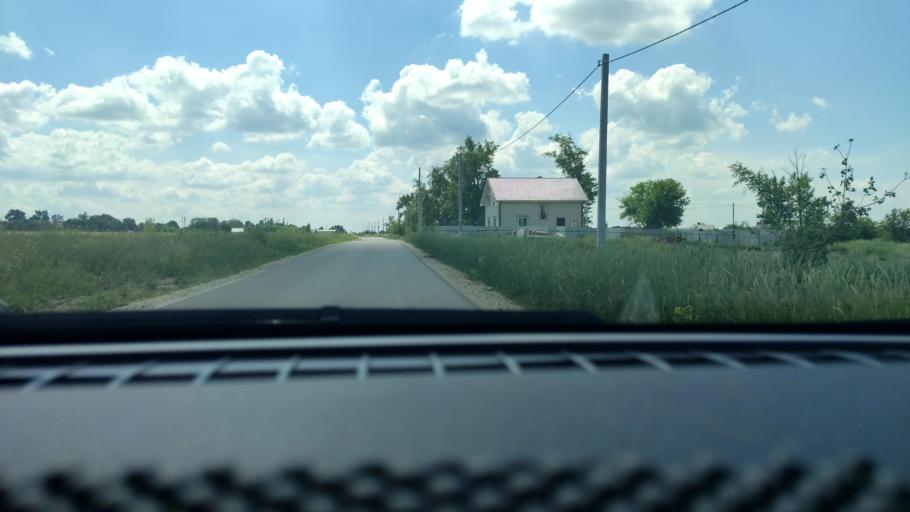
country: RU
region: Voronezj
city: Ramon'
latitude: 51.8978
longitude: 39.1764
